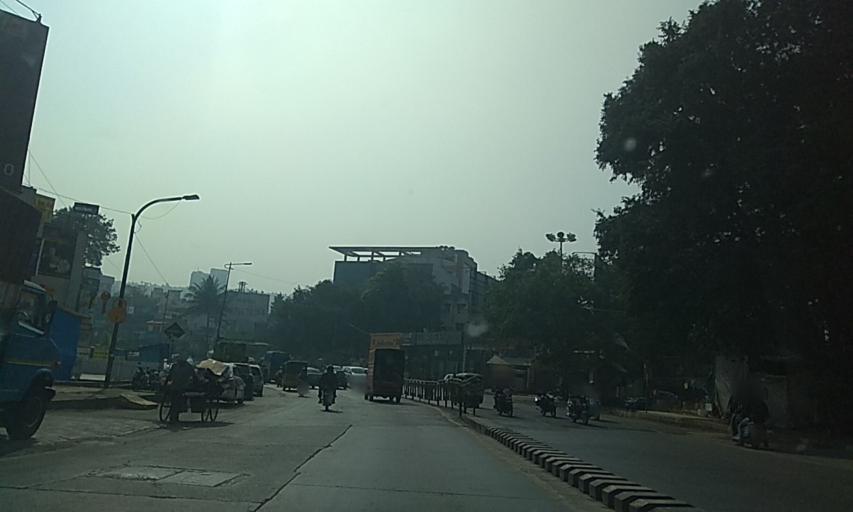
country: IN
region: Maharashtra
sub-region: Pune Division
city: Pimpri
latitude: 18.5625
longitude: 73.7839
